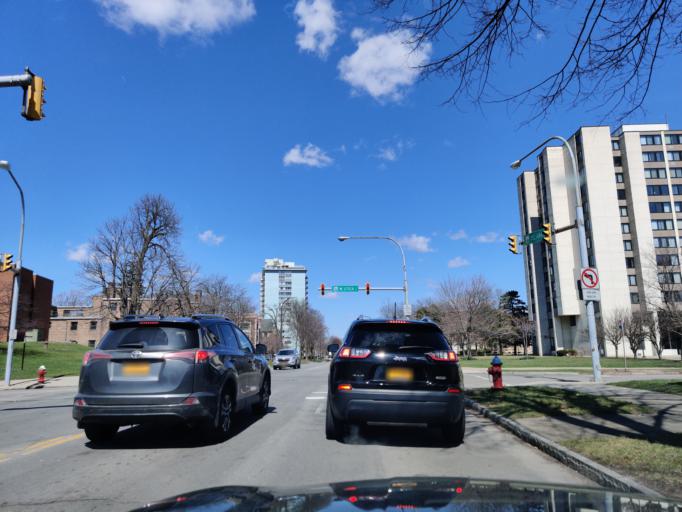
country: US
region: New York
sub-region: Erie County
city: Buffalo
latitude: 42.9111
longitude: -78.8703
